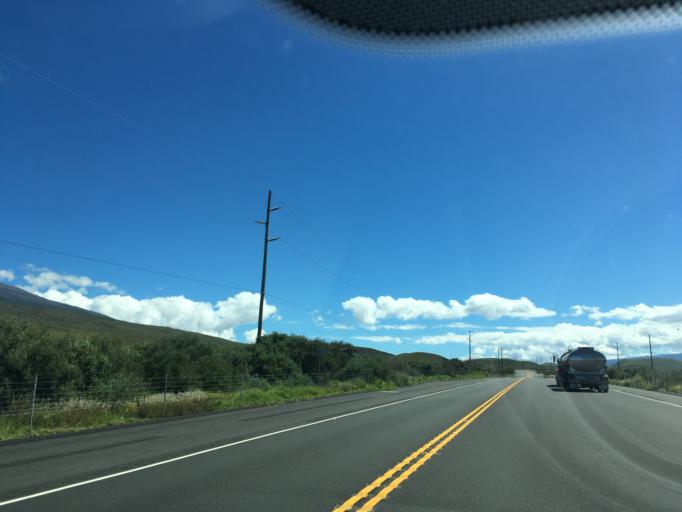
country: US
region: Hawaii
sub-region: Hawaii County
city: Waikoloa
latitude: 19.7882
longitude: -155.6222
